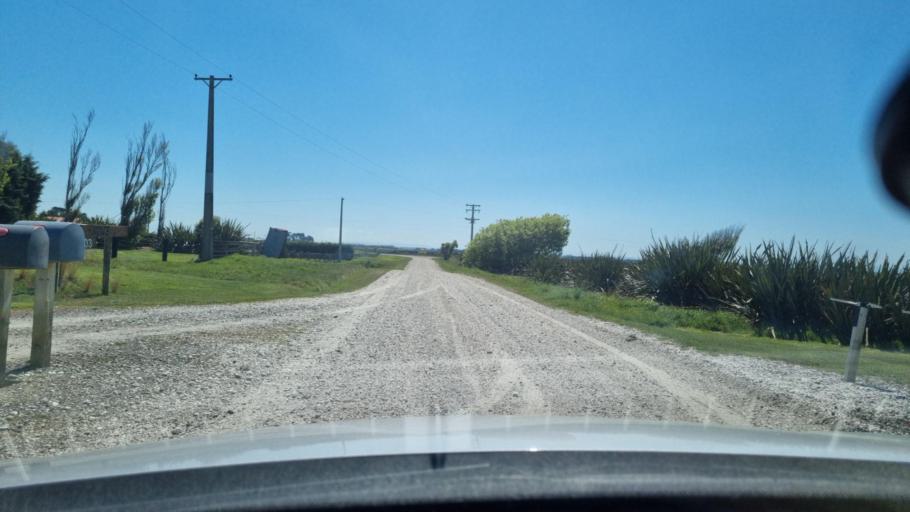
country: NZ
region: Southland
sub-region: Invercargill City
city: Invercargill
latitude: -46.4109
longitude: 168.2634
